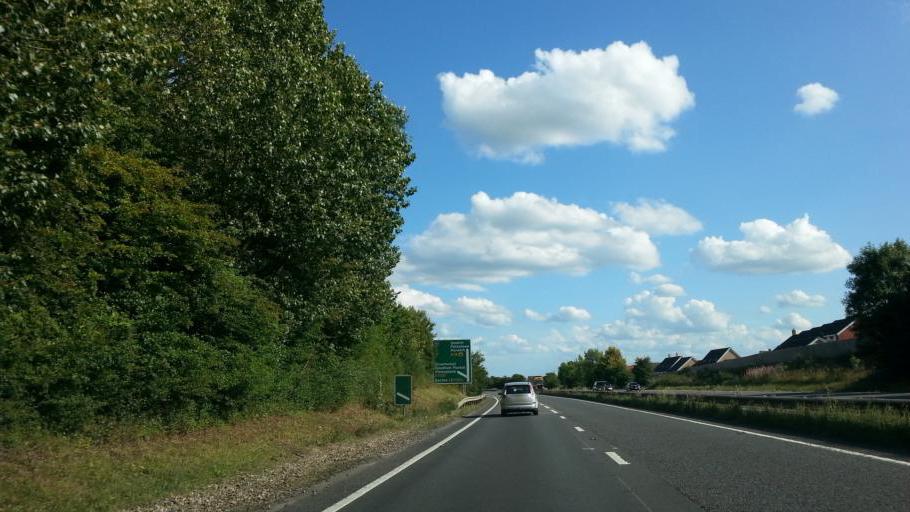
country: GB
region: England
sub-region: Suffolk
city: Stowmarket
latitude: 52.1907
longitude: 1.0169
